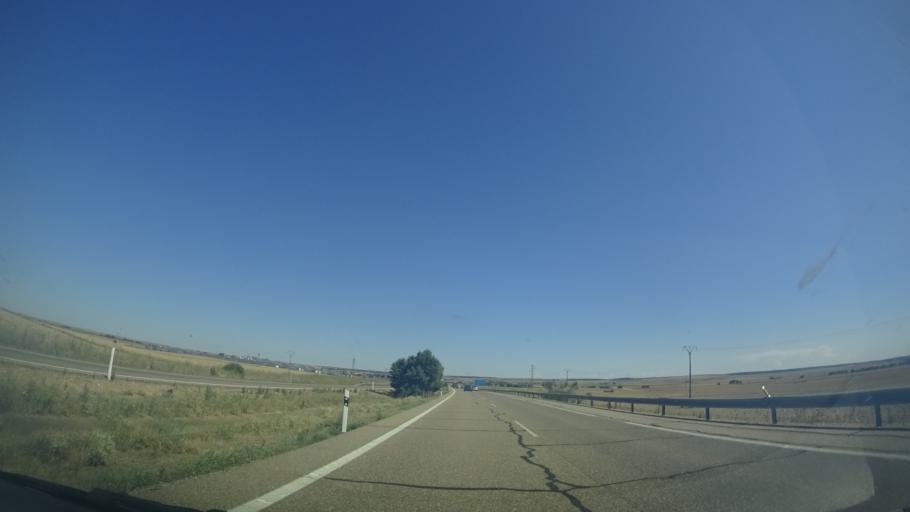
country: ES
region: Castille and Leon
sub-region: Provincia de Zamora
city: Villalpando
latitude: 41.8772
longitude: -5.4497
